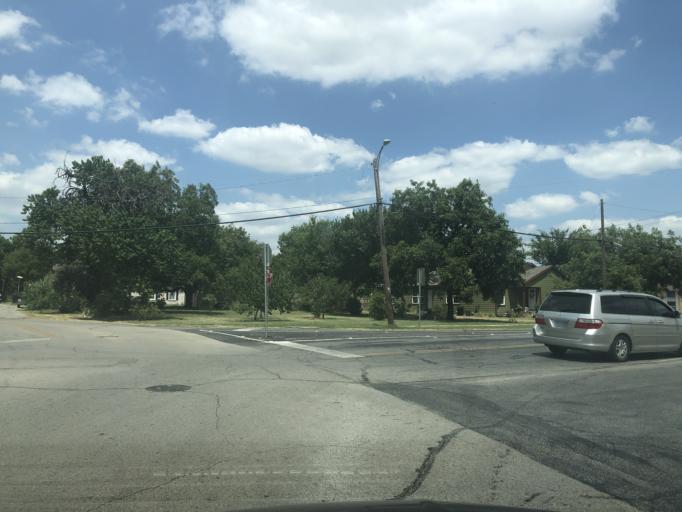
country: US
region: Texas
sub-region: Dallas County
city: Grand Prairie
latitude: 32.7423
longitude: -97.0032
